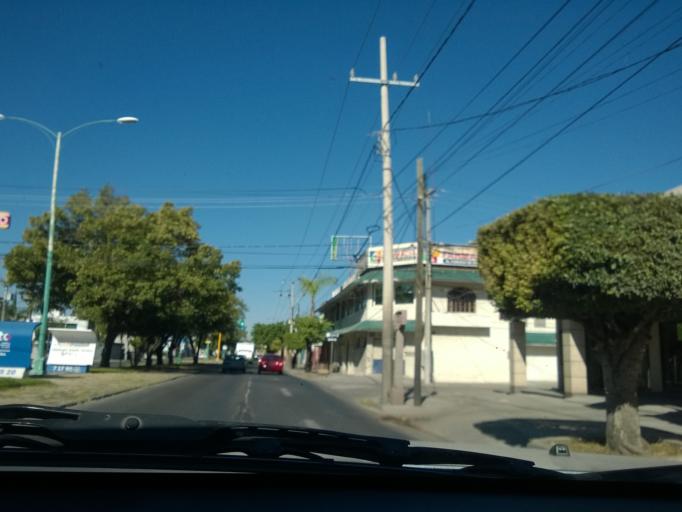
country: MX
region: Guanajuato
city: Leon
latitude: 21.1099
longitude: -101.6685
